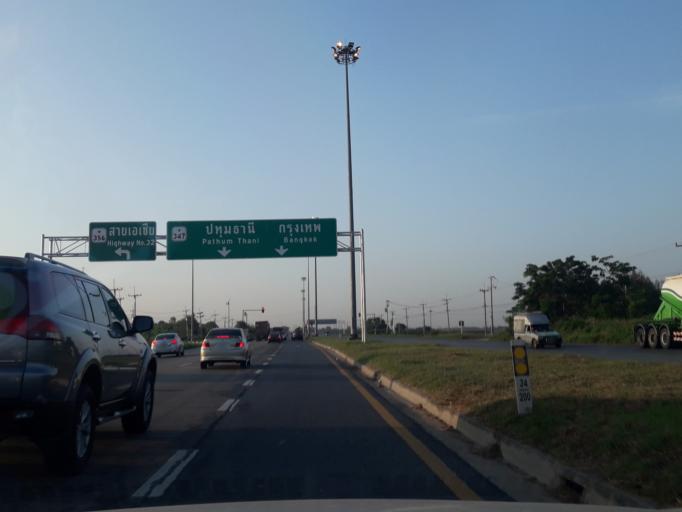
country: TH
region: Phra Nakhon Si Ayutthaya
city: Phra Nakhon Si Ayutthaya
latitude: 14.3083
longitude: 100.5263
